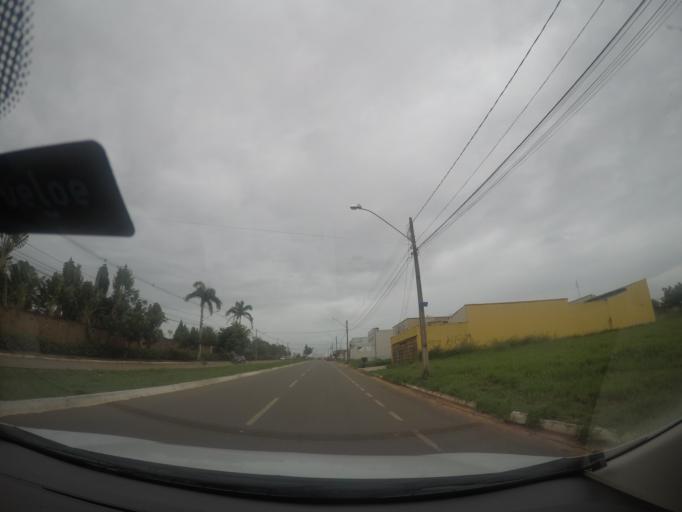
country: BR
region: Goias
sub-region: Goiania
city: Goiania
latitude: -16.6223
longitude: -49.3069
